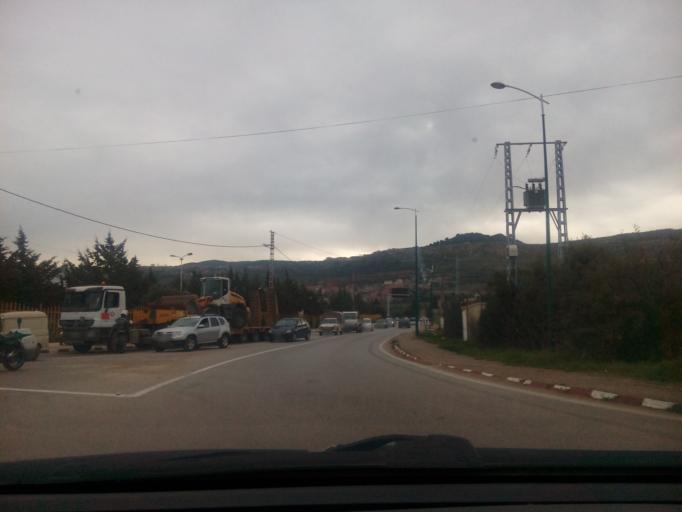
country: DZ
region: Tlemcen
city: Mansoura
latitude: 34.8670
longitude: -1.3492
